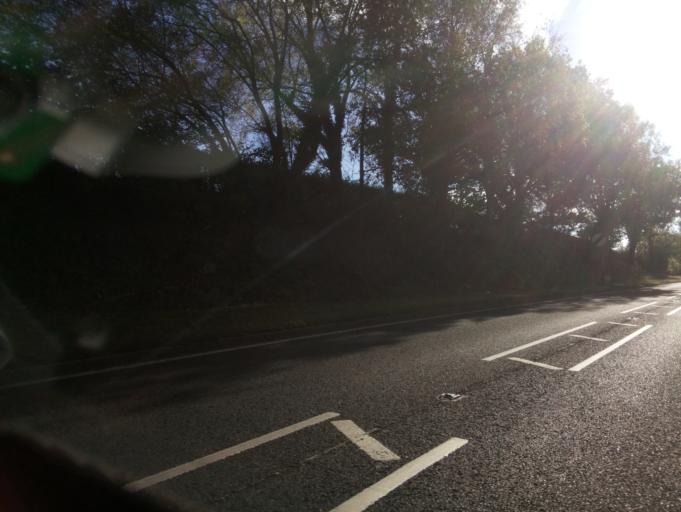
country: GB
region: Wales
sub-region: Sir Powys
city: Brecon
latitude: 51.9186
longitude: -3.4655
